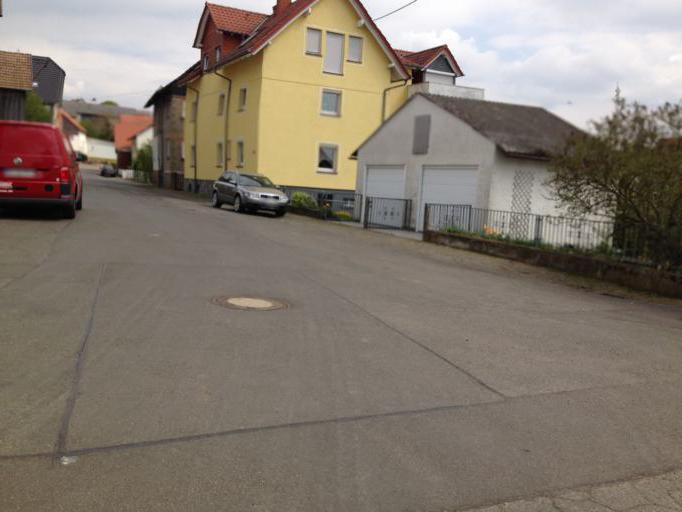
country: DE
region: Hesse
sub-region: Regierungsbezirk Giessen
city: Grunberg
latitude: 50.6105
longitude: 8.9841
